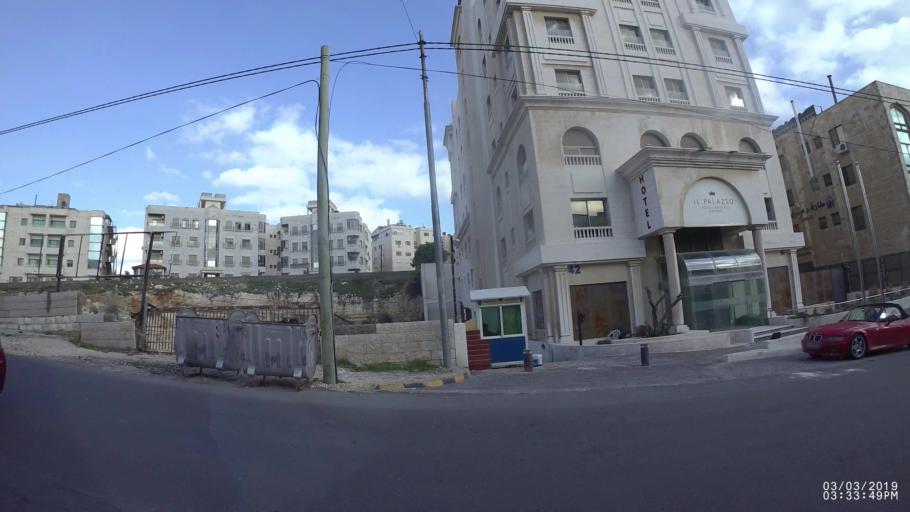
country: JO
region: Amman
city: Al Jubayhah
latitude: 31.9753
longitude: 35.8873
